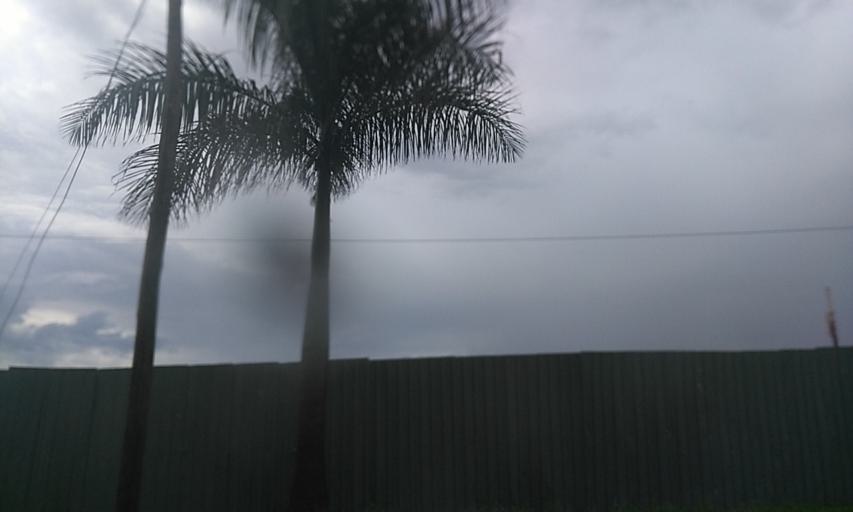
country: UG
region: Central Region
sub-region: Kampala District
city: Kampala
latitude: 0.3276
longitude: 32.5930
